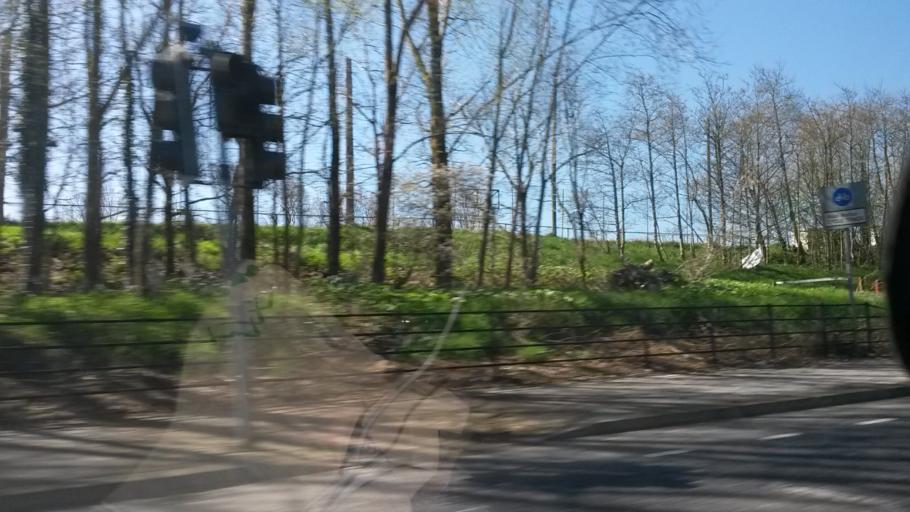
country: IE
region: Munster
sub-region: County Cork
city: Blarney
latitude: 51.8947
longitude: -8.5266
